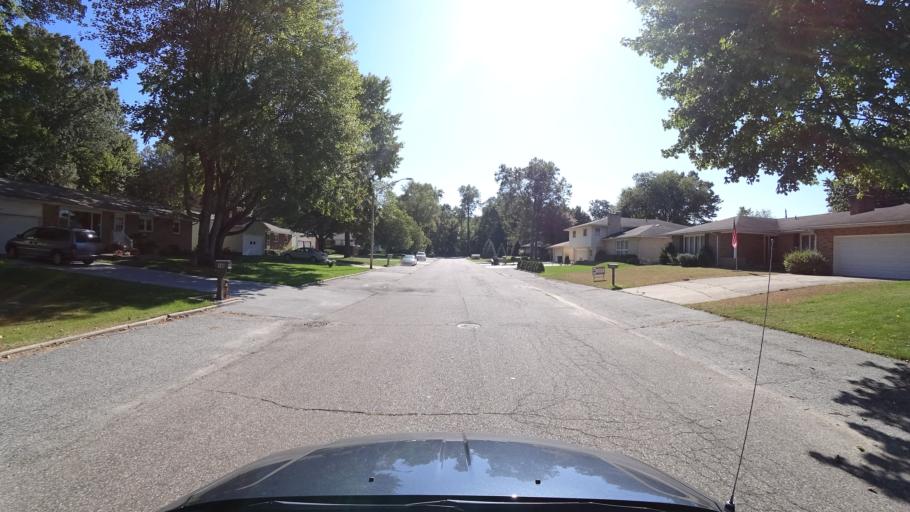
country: US
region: Indiana
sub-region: LaPorte County
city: Michigan City
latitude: 41.6924
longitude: -86.8829
